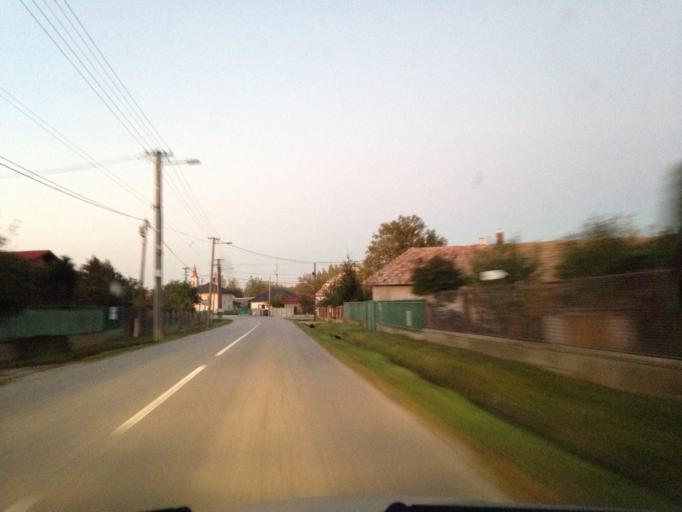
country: SK
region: Nitriansky
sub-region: Okres Komarno
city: Hurbanovo
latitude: 47.9004
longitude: 18.3067
